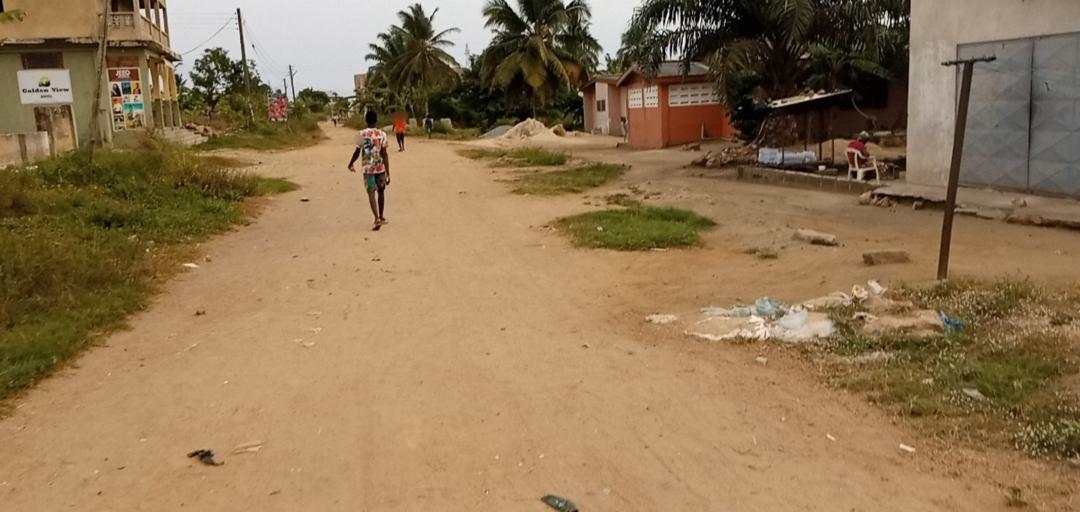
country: GH
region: Central
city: Winneba
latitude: 5.3580
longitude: -0.6302
